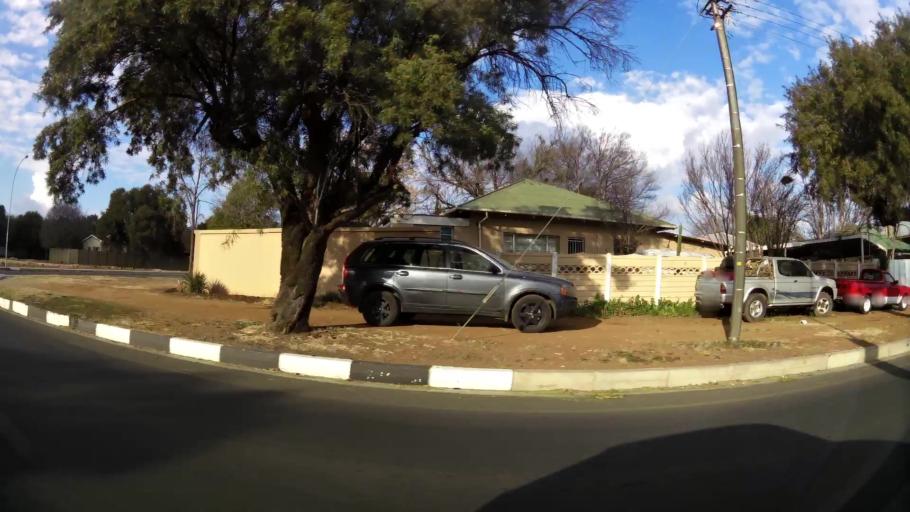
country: ZA
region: Orange Free State
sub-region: Mangaung Metropolitan Municipality
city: Bloemfontein
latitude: -29.1003
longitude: 26.2049
